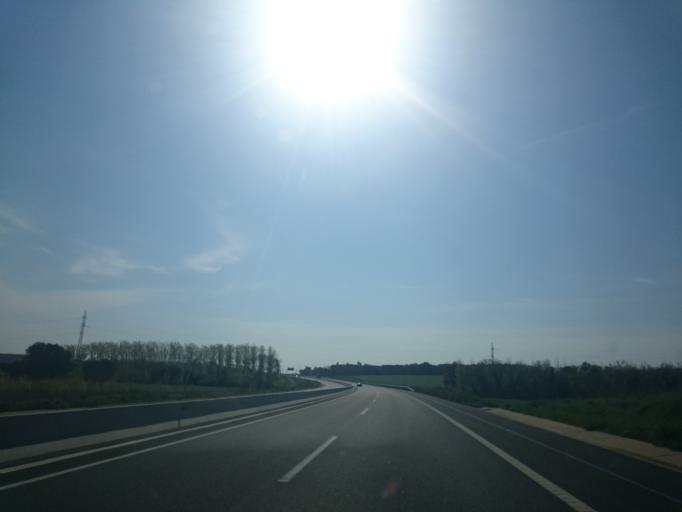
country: ES
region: Catalonia
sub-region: Provincia de Girona
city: Vilobi d'Onyar
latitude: 41.8702
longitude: 2.7659
